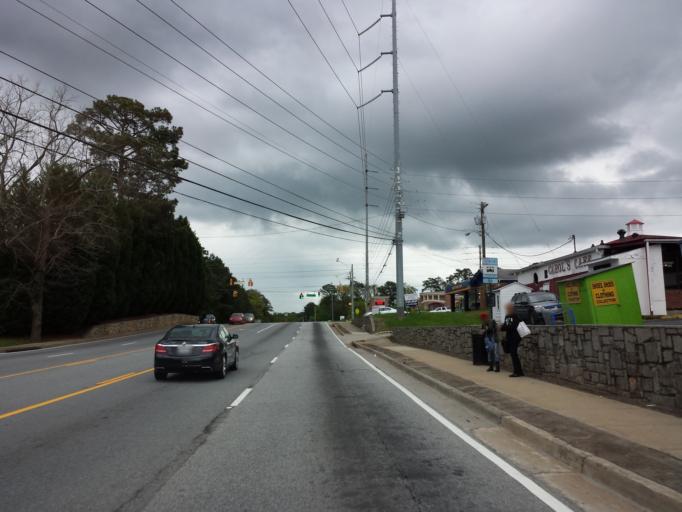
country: US
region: Georgia
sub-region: Cobb County
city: Marietta
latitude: 34.0138
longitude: -84.5498
